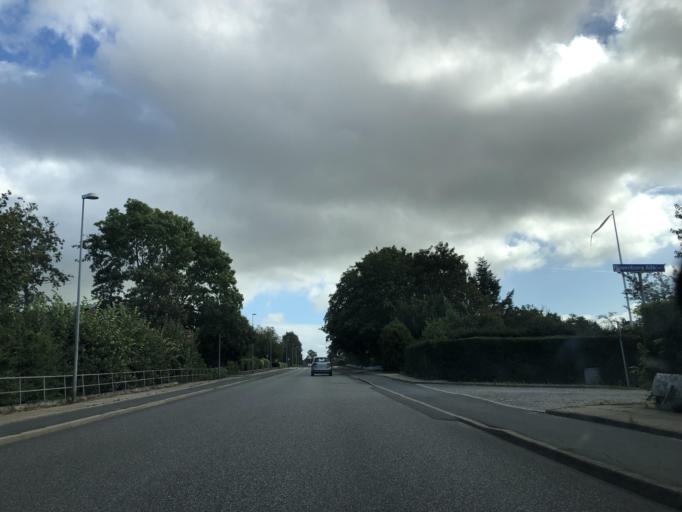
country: DK
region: Central Jutland
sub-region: Randers Kommune
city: Randers
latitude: 56.4727
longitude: 10.0126
